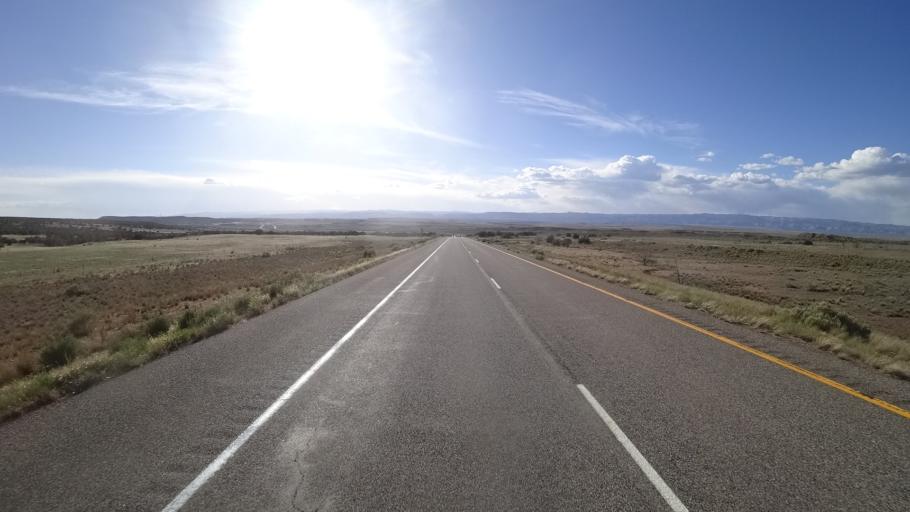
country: US
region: Colorado
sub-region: Mesa County
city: Loma
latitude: 39.1910
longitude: -109.0452
